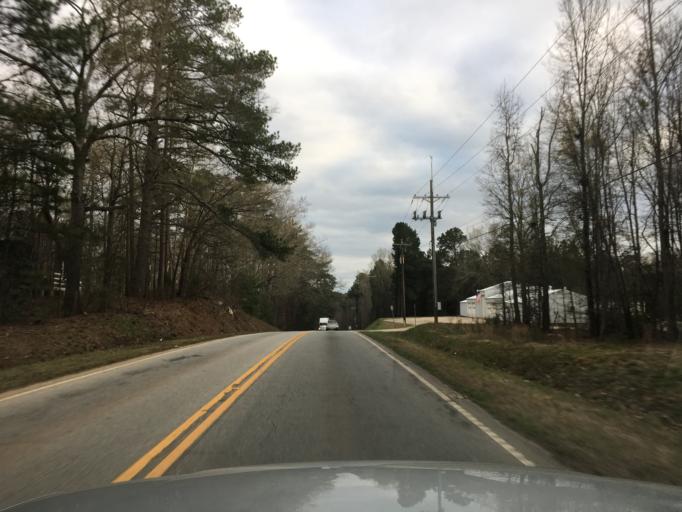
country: US
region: South Carolina
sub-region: Saluda County
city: Saluda
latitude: 33.9927
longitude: -81.7711
